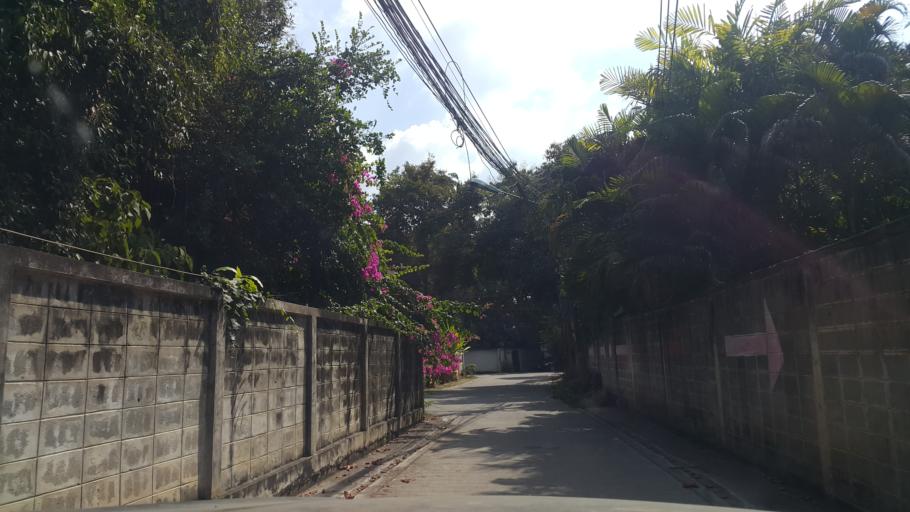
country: TH
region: Chiang Mai
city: Chiang Mai
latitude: 18.7914
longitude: 99.0195
